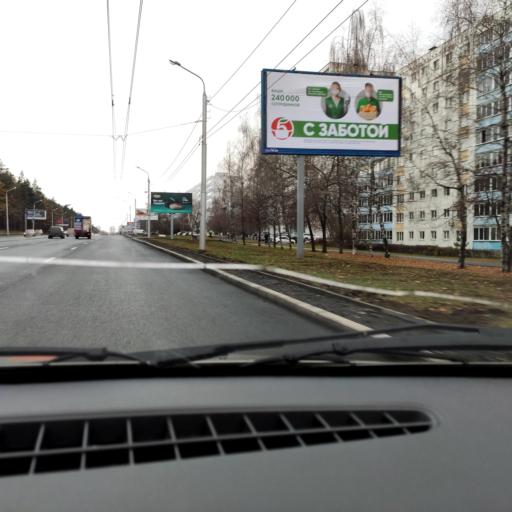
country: RU
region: Bashkortostan
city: Ufa
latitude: 54.7477
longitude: 56.0304
